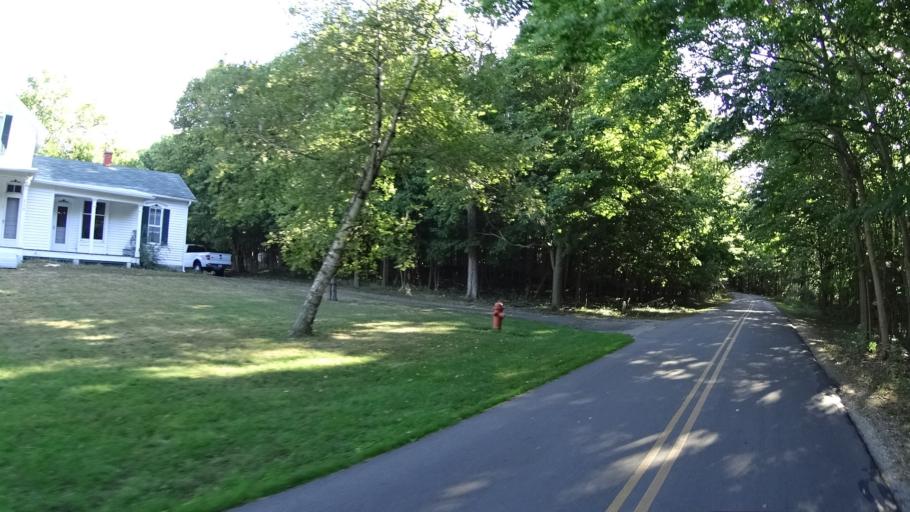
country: US
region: Ohio
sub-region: Erie County
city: Sandusky
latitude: 41.6129
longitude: -82.7194
